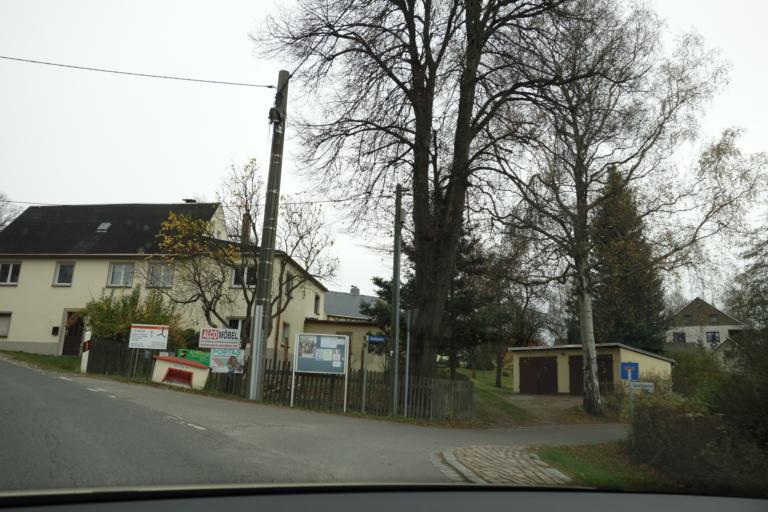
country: DE
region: Saxony
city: Leubsdorf
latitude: 50.7986
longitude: 13.1825
